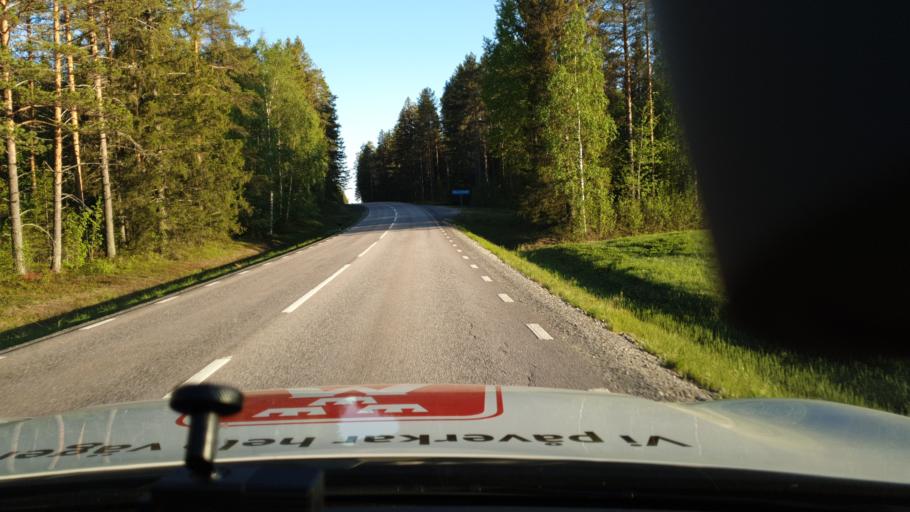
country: SE
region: Vaesterbotten
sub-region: Umea Kommun
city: Ersmark
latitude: 63.9415
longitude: 20.3040
